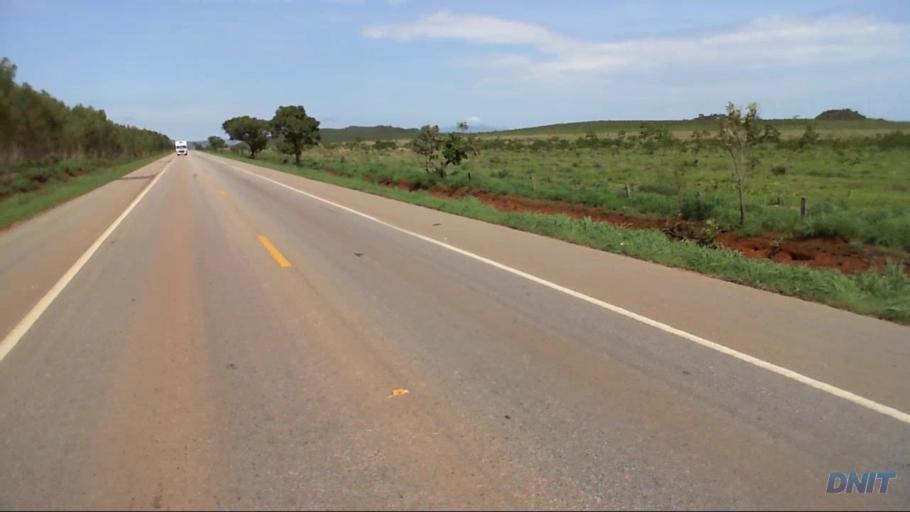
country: BR
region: Goias
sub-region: Barro Alto
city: Barro Alto
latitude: -15.2046
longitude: -48.7335
